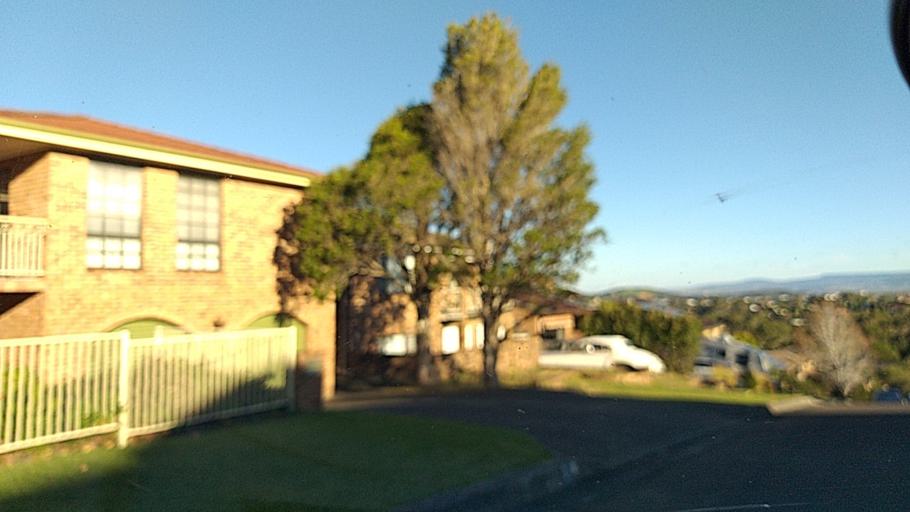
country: AU
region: New South Wales
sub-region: Wollongong
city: Mount Keira
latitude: -34.4217
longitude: 150.8502
